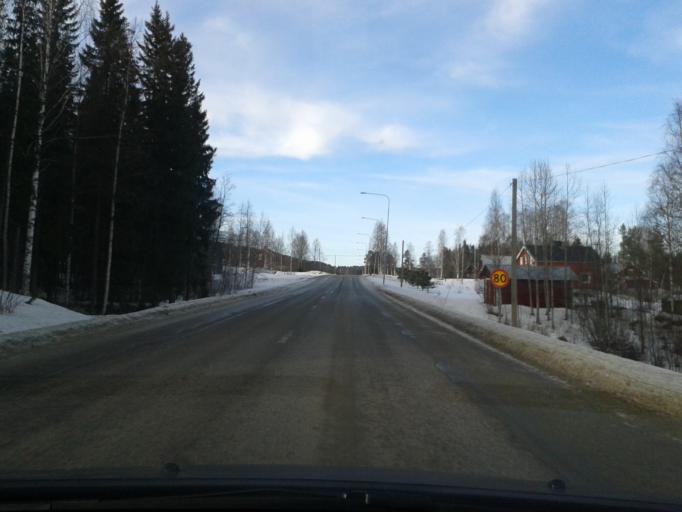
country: SE
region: Vaesternorrland
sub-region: OErnskoeldsviks Kommun
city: Bredbyn
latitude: 63.4748
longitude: 18.0961
